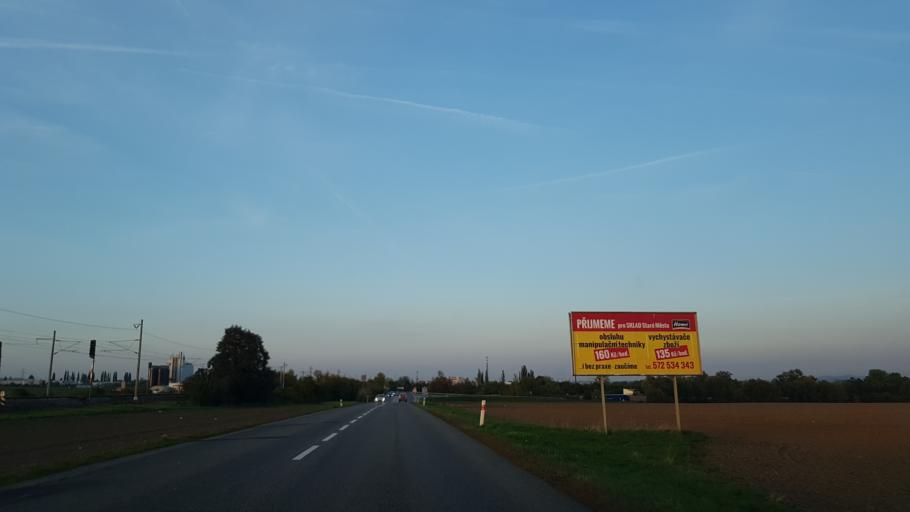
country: CZ
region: Zlin
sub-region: Okres Uherske Hradiste
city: Stare Mesto
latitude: 49.0618
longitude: 17.4077
